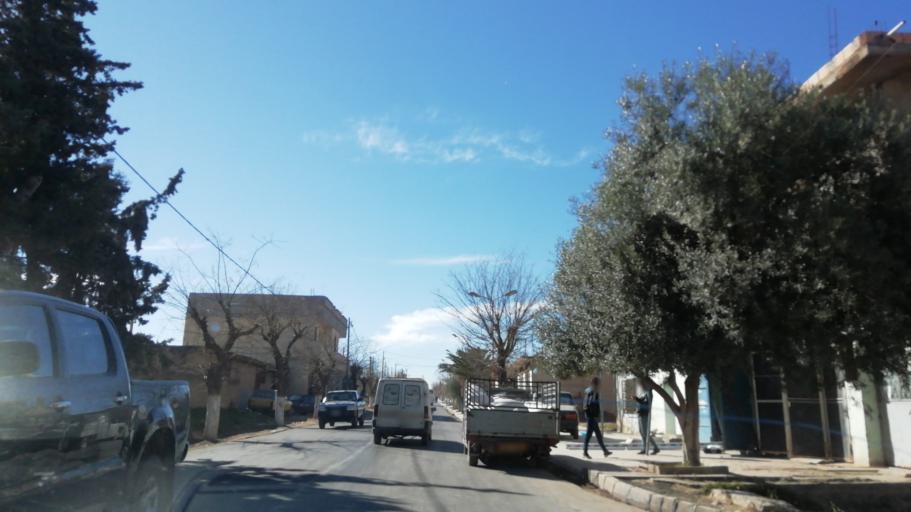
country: DZ
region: Tlemcen
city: Sebdou
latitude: 34.6521
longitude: -1.3183
